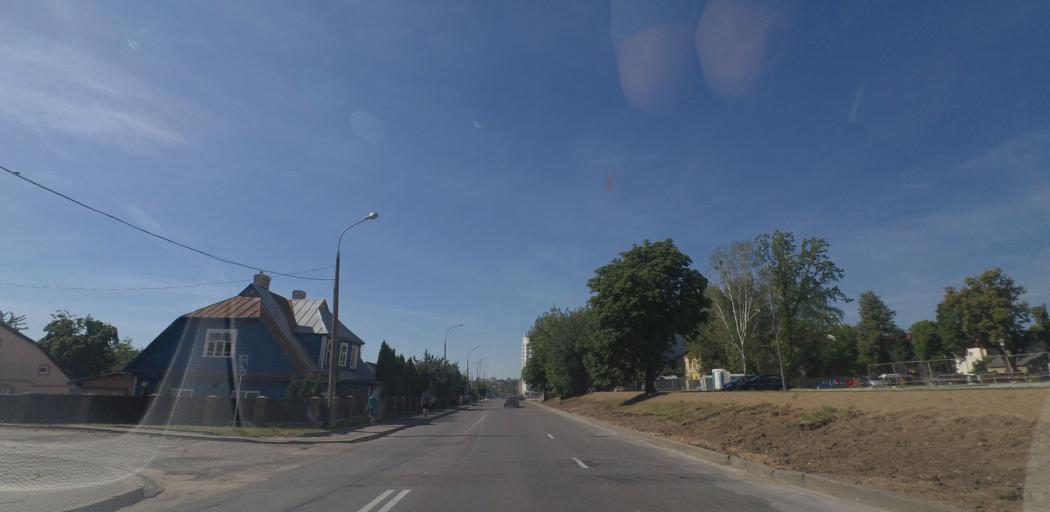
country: BY
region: Grodnenskaya
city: Hrodna
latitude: 53.6770
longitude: 23.8540
